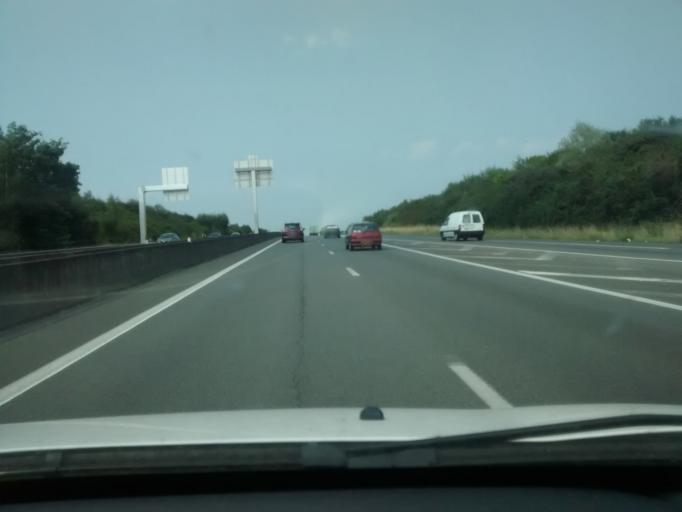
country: FR
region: Pays de la Loire
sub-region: Departement de la Loire-Atlantique
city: Saint-Nazaire
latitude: 47.2861
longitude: -2.2536
